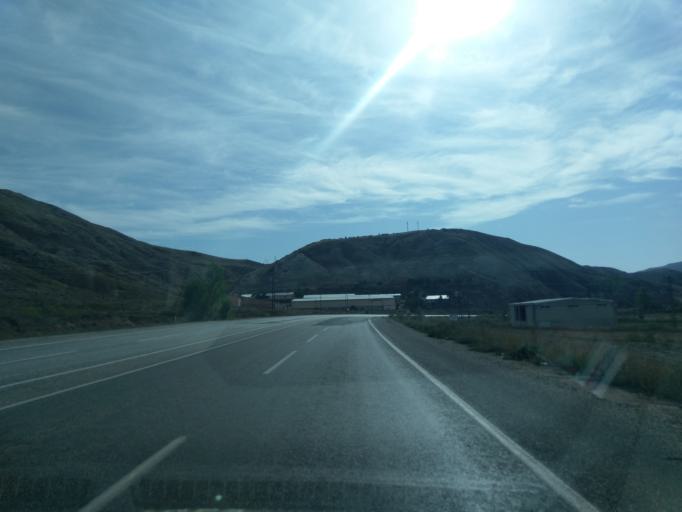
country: TR
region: Sivas
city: Zara
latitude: 39.8593
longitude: 37.8348
